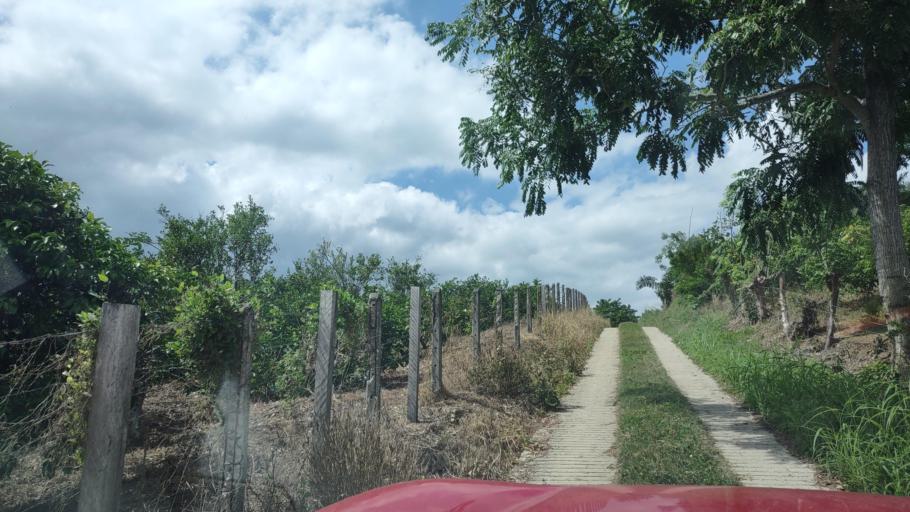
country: MX
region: Puebla
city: San Jose Acateno
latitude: 20.2221
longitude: -97.1500
